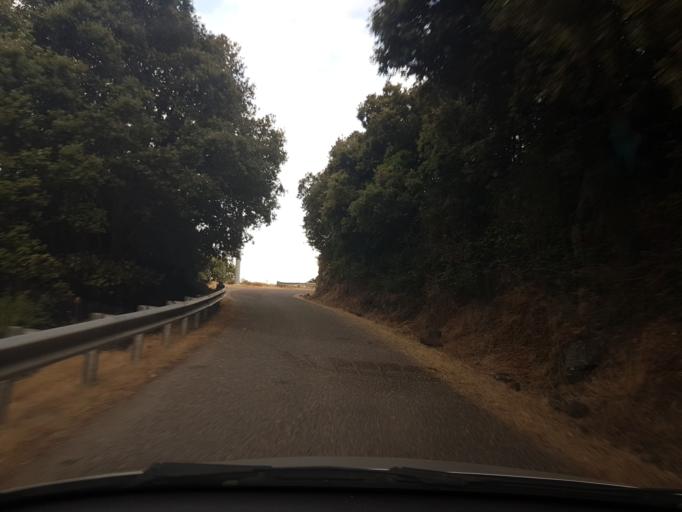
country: IT
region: Sardinia
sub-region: Provincia di Oristano
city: Seneghe
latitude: 40.1097
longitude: 8.6059
